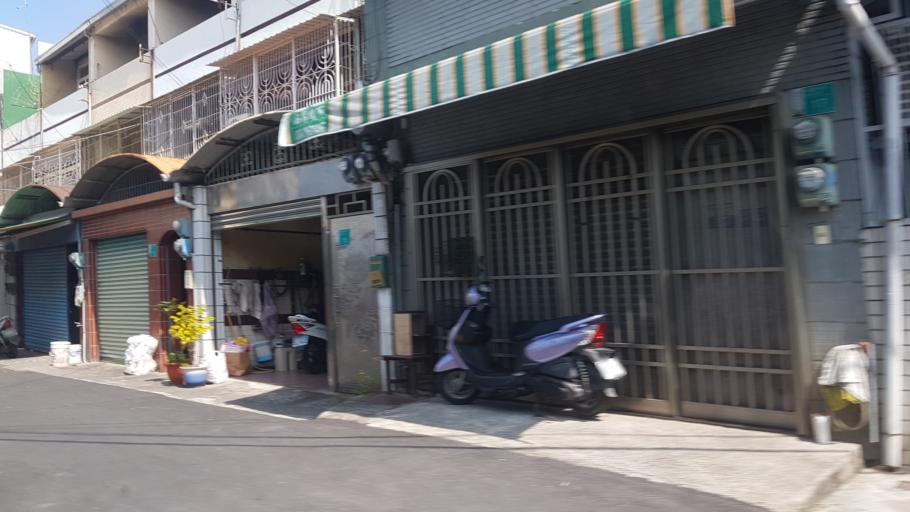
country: TW
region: Taiwan
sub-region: Tainan
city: Tainan
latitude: 22.9371
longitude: 120.2480
